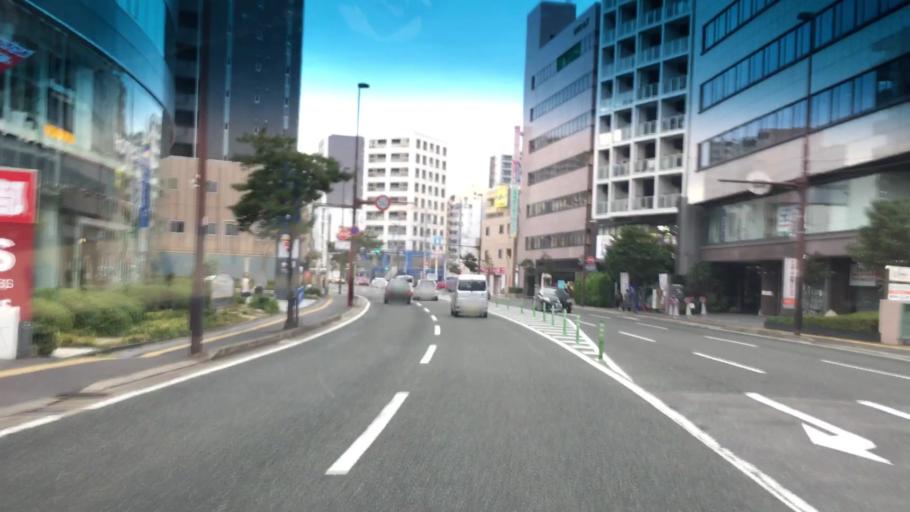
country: JP
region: Fukuoka
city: Fukuoka-shi
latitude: 33.5817
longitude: 130.4006
